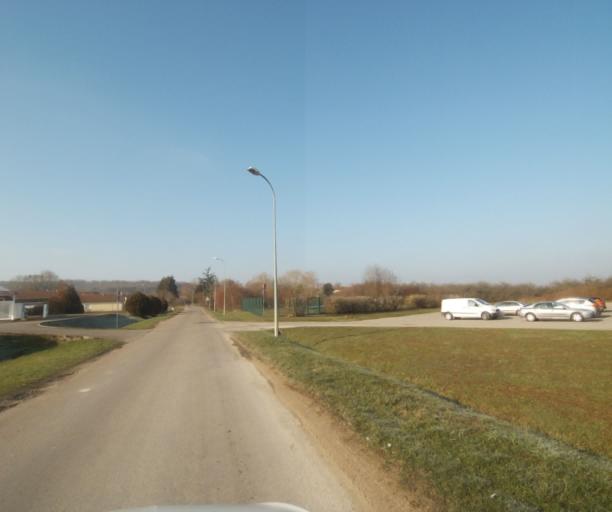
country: FR
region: Champagne-Ardenne
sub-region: Departement de la Haute-Marne
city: Wassy
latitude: 48.5007
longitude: 4.9370
